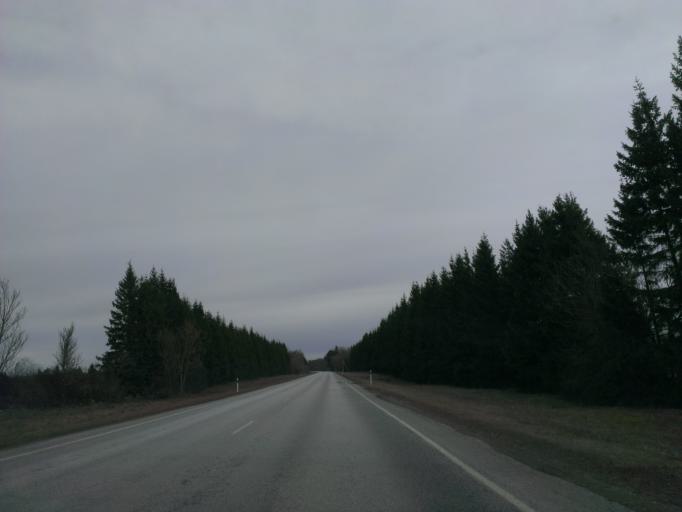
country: EE
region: Laeaene
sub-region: Lihula vald
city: Lihula
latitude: 58.6097
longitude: 23.5723
